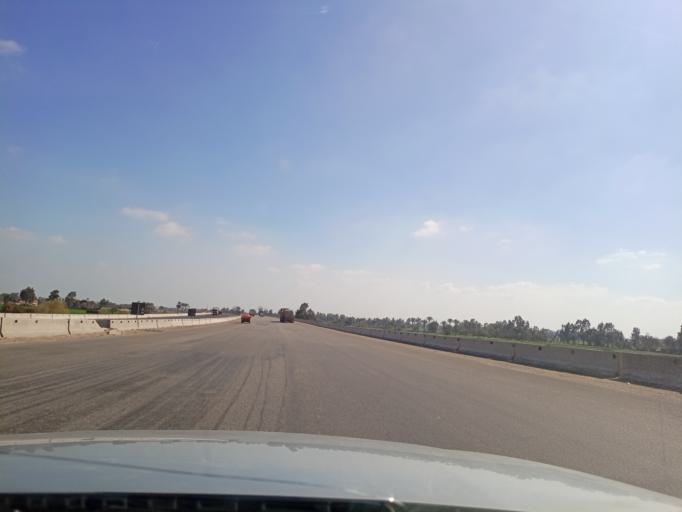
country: EG
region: Eastern Province
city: Mashtul as Suq
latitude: 30.4594
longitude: 31.3362
